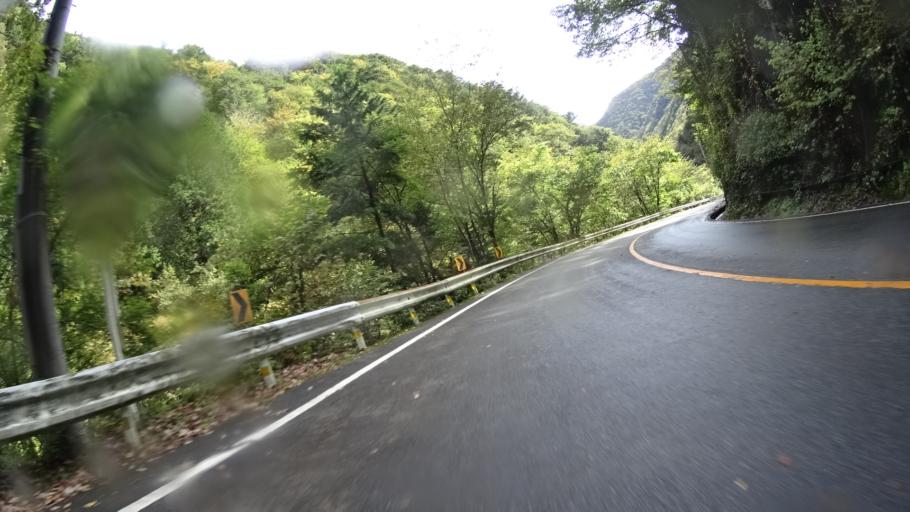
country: JP
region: Yamanashi
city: Enzan
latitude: 35.7981
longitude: 138.8952
